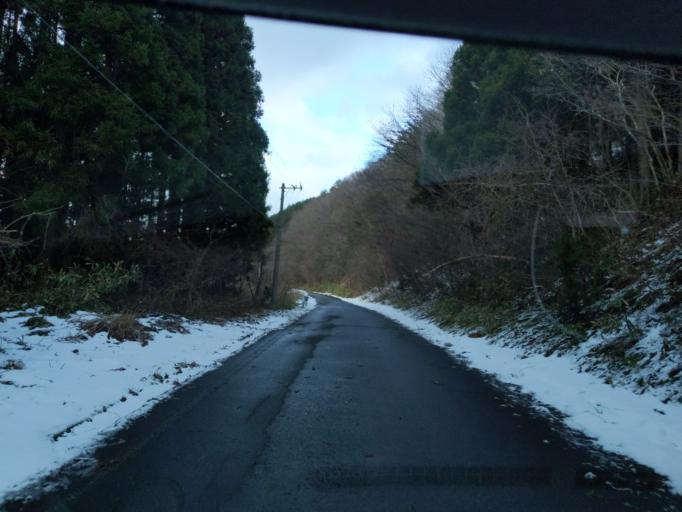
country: JP
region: Iwate
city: Ichinoseki
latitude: 39.0137
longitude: 140.9759
